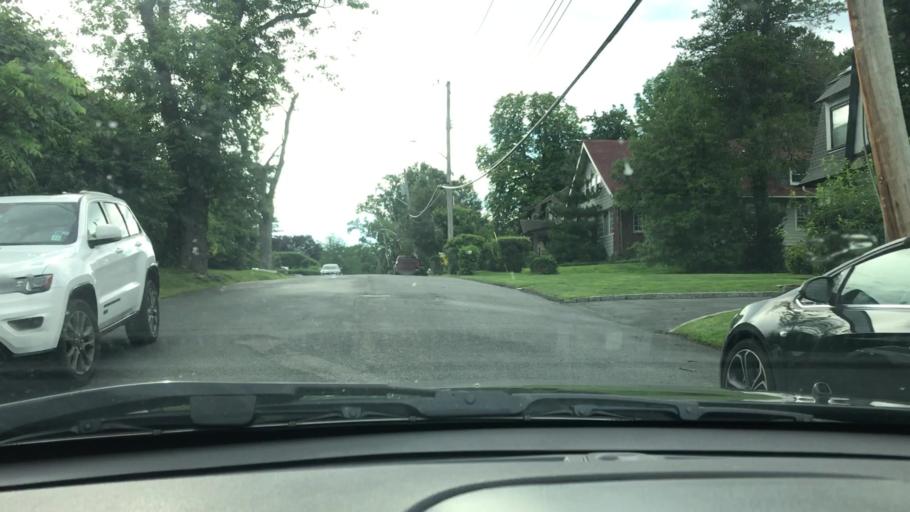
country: US
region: New York
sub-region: Westchester County
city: New Rochelle
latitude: 40.9350
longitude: -73.7936
